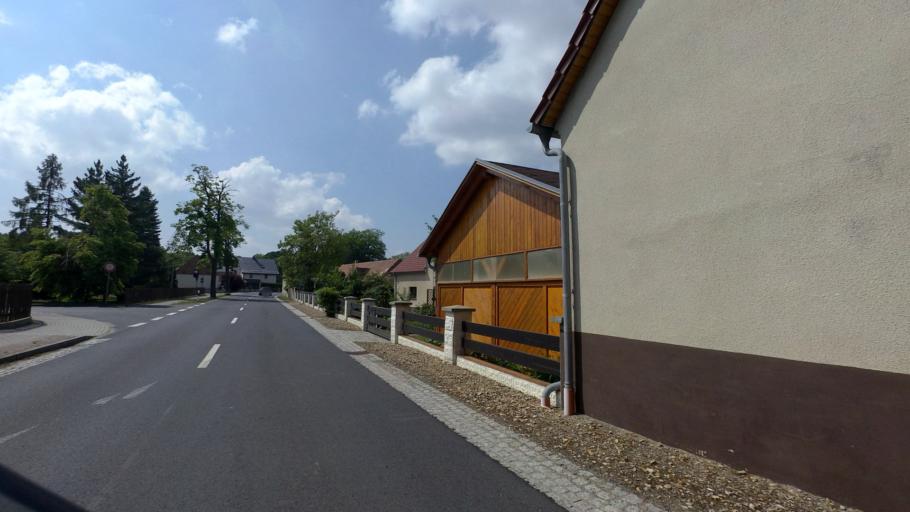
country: DE
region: Saxony
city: Mucka
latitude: 51.3154
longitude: 14.7045
